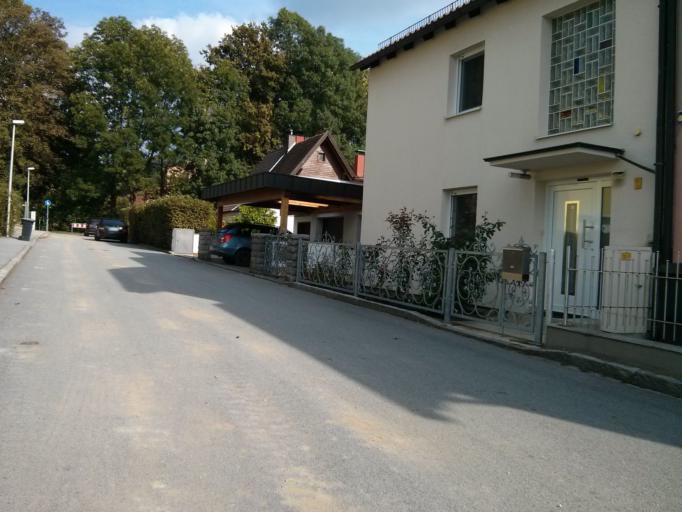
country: DE
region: Bavaria
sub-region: Lower Bavaria
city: Deggendorf
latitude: 48.8451
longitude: 12.9756
